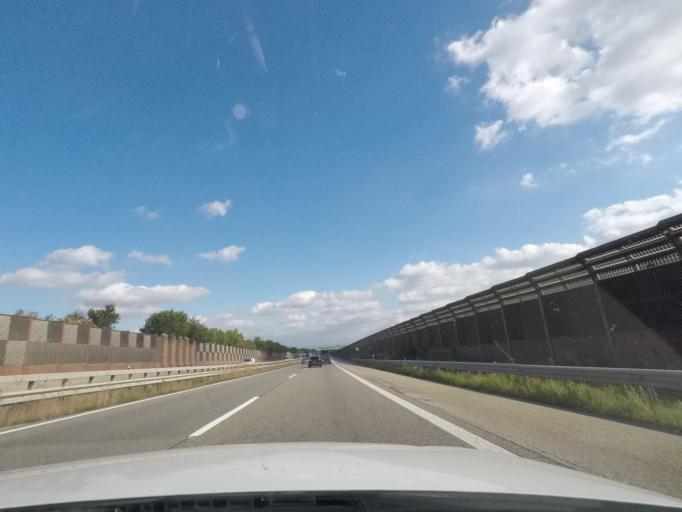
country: DE
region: Rheinland-Pfalz
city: Grunstadt
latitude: 49.5549
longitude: 8.1571
